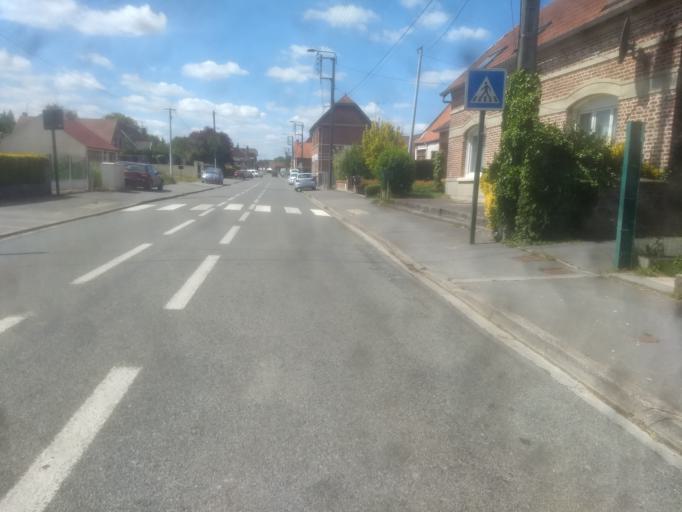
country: FR
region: Nord-Pas-de-Calais
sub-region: Departement du Pas-de-Calais
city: Dainville
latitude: 50.2489
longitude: 2.7282
